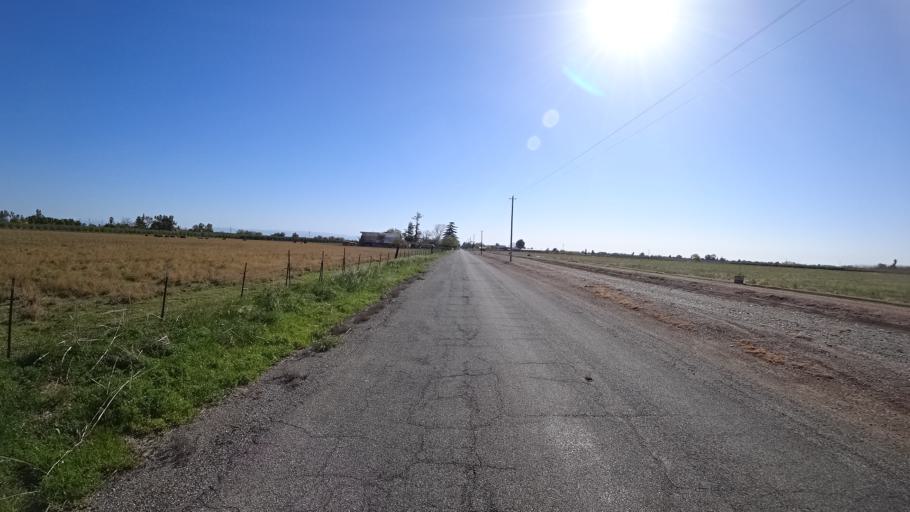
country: US
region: California
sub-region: Glenn County
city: Orland
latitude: 39.7442
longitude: -122.2426
